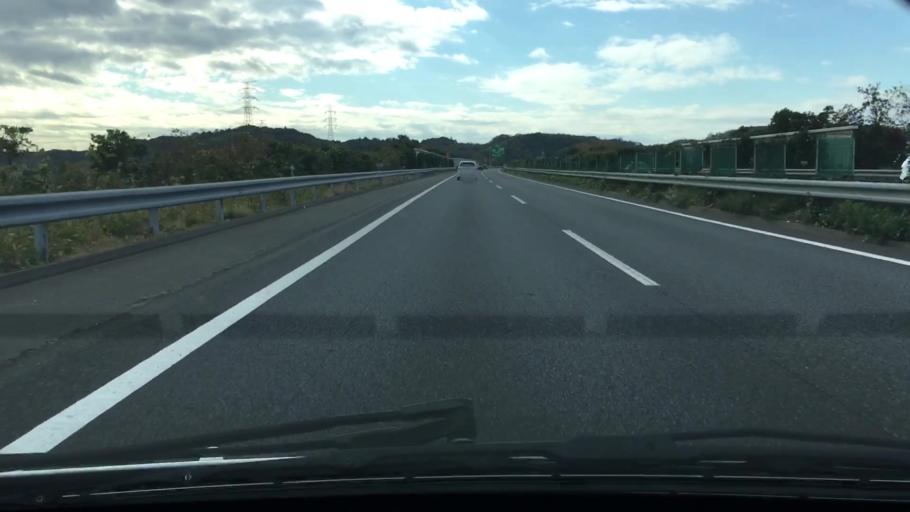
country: JP
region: Chiba
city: Kisarazu
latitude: 35.3972
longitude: 140.0055
